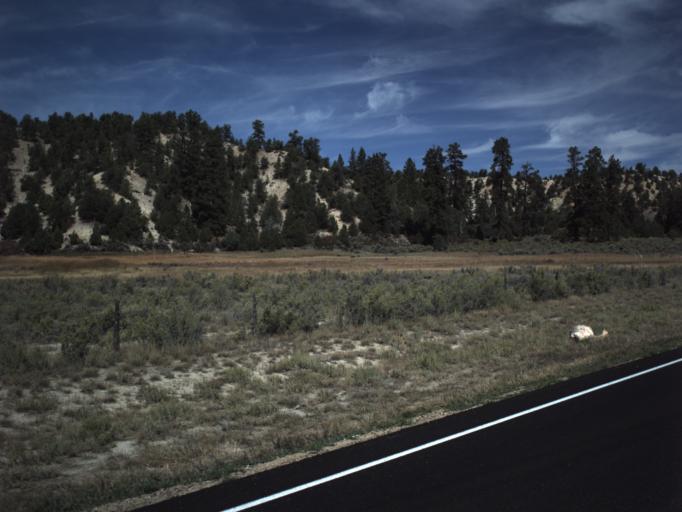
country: US
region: Utah
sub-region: Garfield County
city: Panguitch
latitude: 37.7074
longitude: -111.7886
